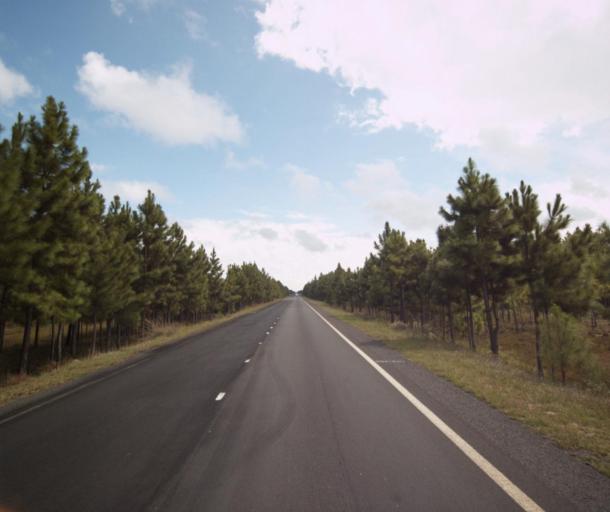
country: BR
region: Rio Grande do Sul
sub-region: Tapes
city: Tapes
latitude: -31.4154
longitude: -51.1735
